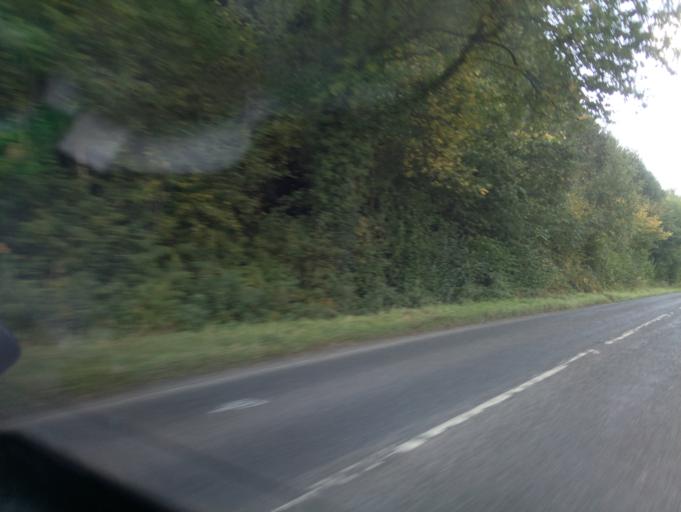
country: GB
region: England
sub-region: Herefordshire
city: Moccas
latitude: 52.1027
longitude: -2.9473
